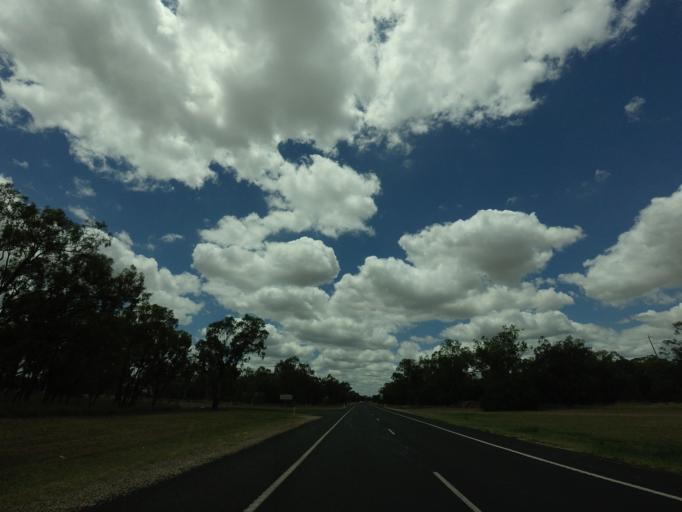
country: AU
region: Queensland
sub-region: Goondiwindi
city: Goondiwindi
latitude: -28.0772
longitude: 150.7434
